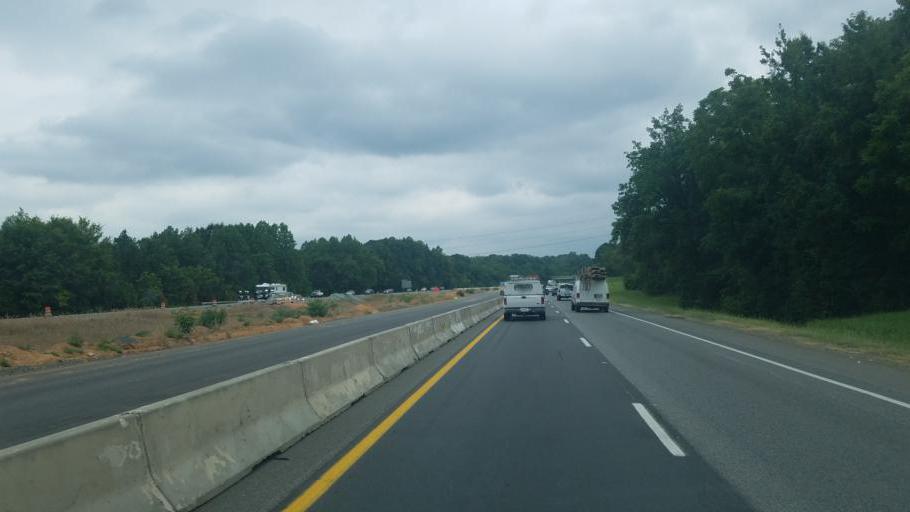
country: US
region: North Carolina
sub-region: Mecklenburg County
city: Cornelius
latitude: 35.4573
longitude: -80.8731
